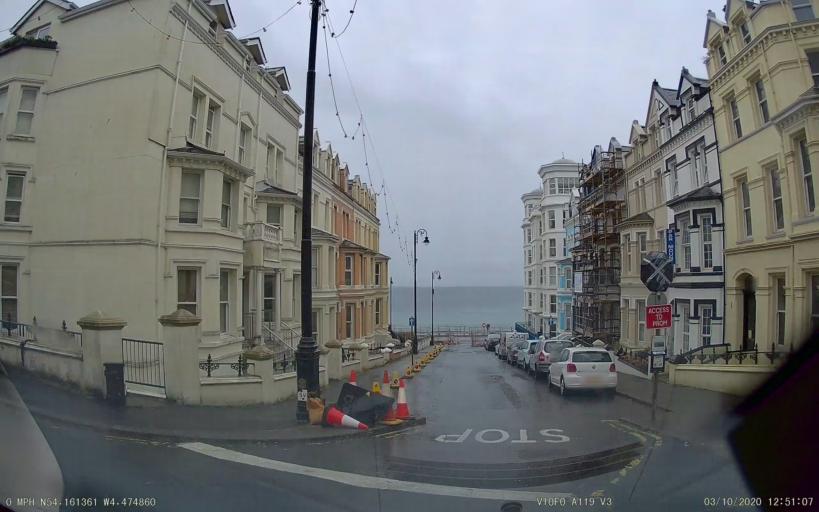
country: IM
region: Douglas
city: Douglas
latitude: 54.1614
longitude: -4.4749
